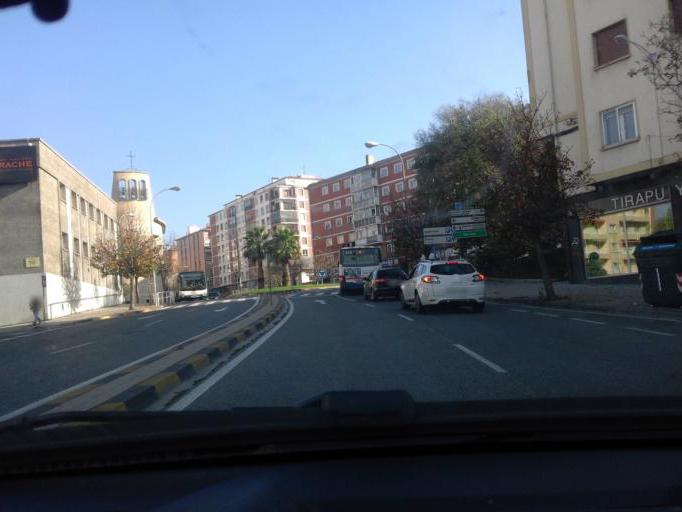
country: ES
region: Navarre
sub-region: Provincia de Navarra
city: Ermitagana
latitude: 42.8155
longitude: -1.6659
